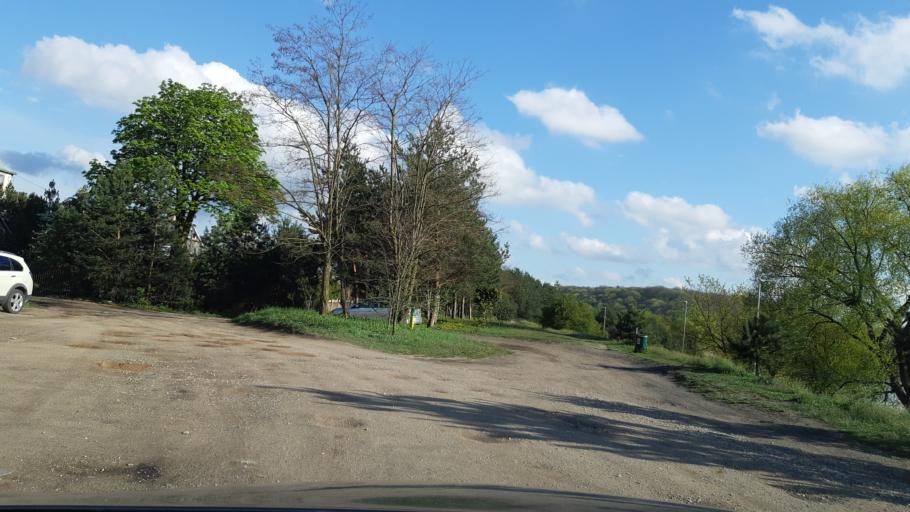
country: LT
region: Kauno apskritis
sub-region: Kaunas
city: Aleksotas
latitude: 54.8668
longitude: 23.9302
